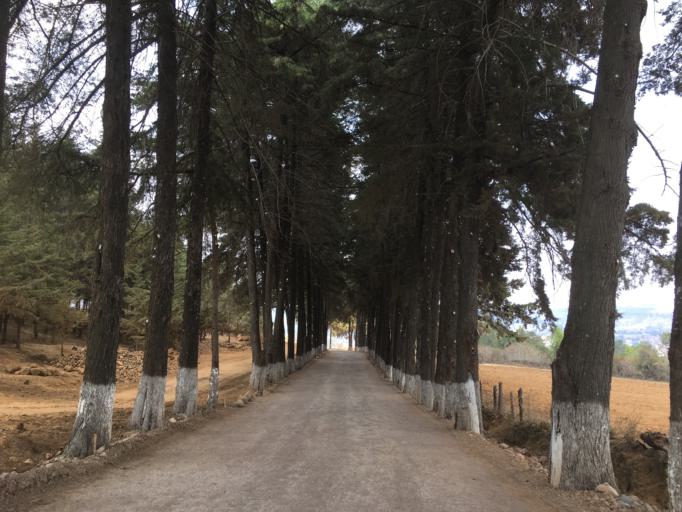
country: MX
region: Michoacan
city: Patzcuaro
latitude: 19.5146
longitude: -101.6300
